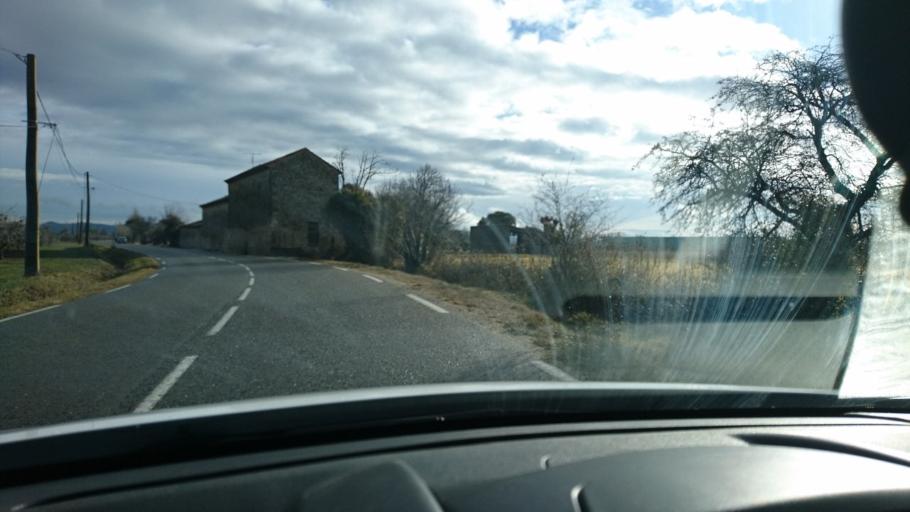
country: FR
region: Languedoc-Roussillon
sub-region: Departement du Gard
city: Pont-Saint-Esprit
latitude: 44.2581
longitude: 4.6692
